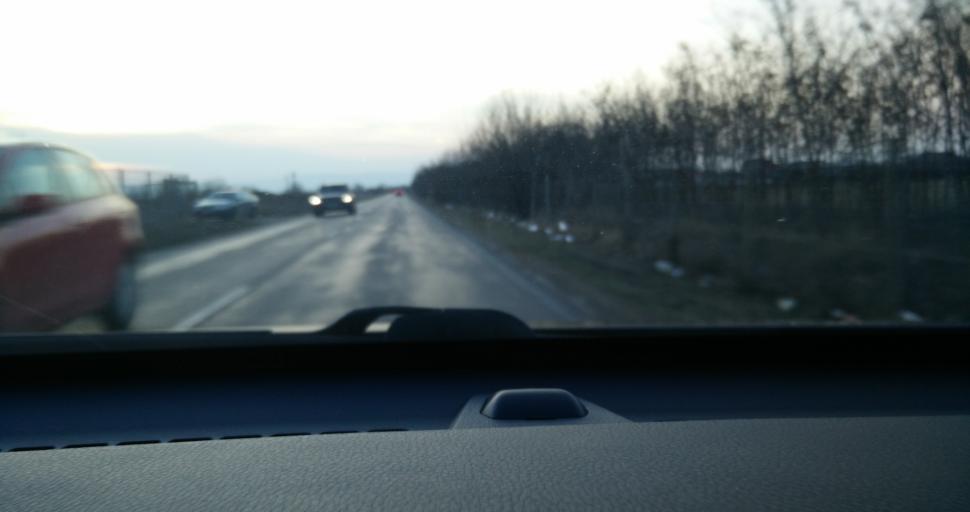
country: RO
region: Vrancea
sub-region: Comuna Milcovul
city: Milcovul
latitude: 45.6773
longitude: 27.2418
